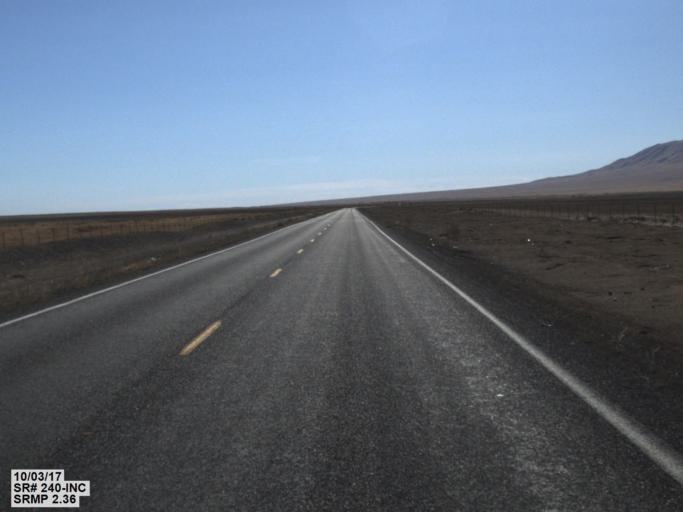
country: US
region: Washington
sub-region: Grant County
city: Desert Aire
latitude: 46.5524
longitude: -119.6978
